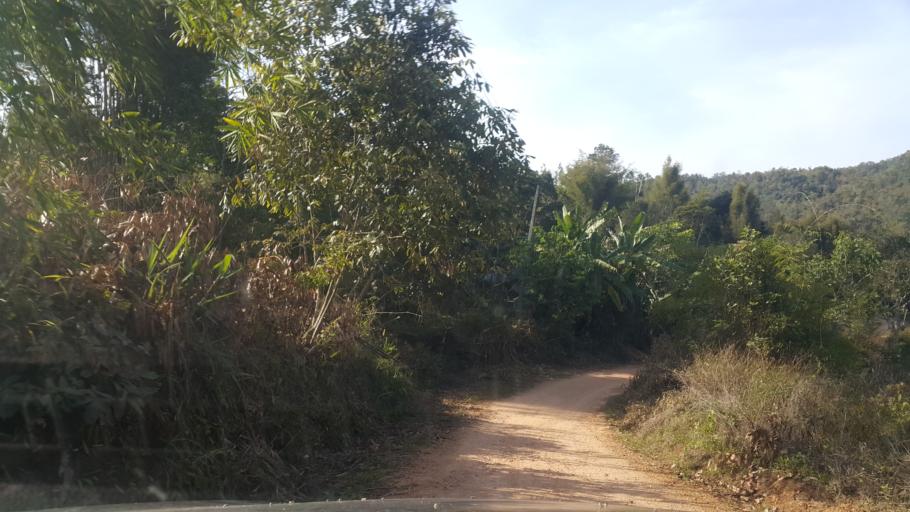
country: TH
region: Chiang Mai
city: Samoeng
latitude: 18.9588
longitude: 98.6730
